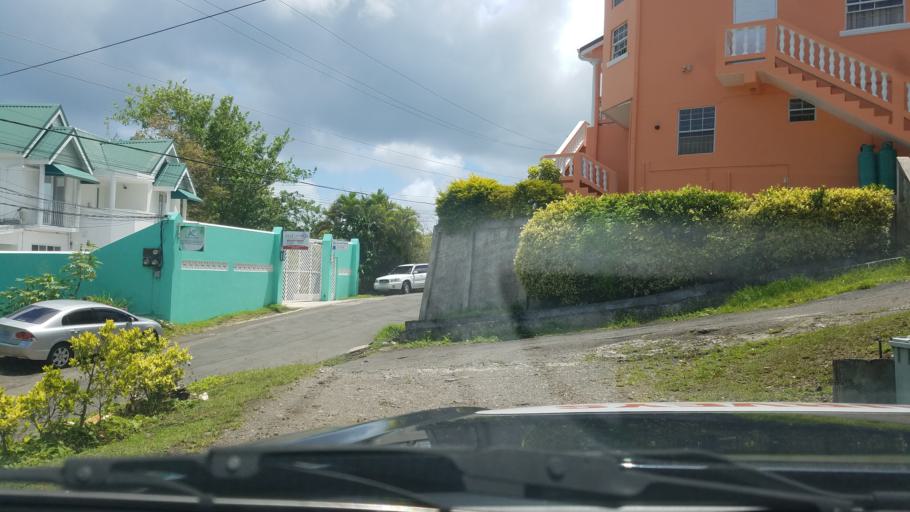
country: LC
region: Castries Quarter
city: Castries
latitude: 14.0142
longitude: -61.0046
